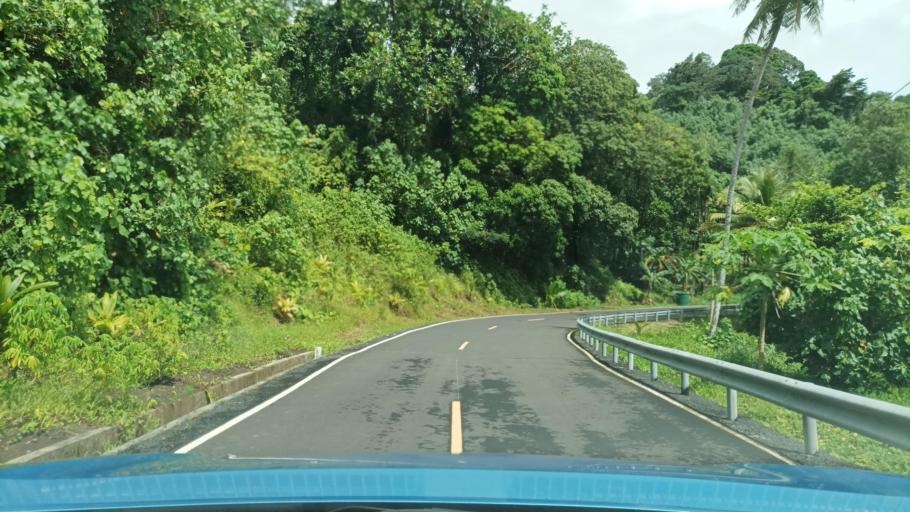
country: FM
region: Pohnpei
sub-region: Madolenihm Municipality
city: Madolenihm Municipality Government
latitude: 6.8625
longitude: 158.3243
